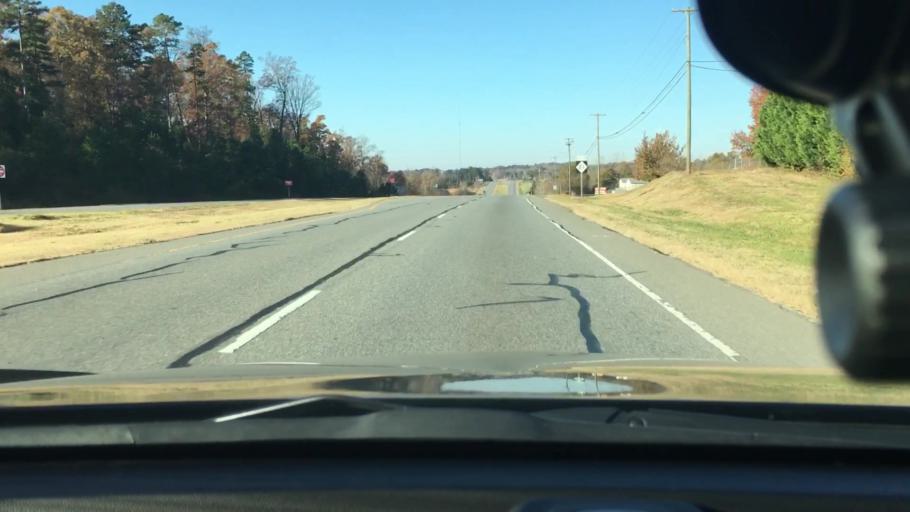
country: US
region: North Carolina
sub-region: Cabarrus County
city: Concord
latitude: 35.3719
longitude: -80.5583
